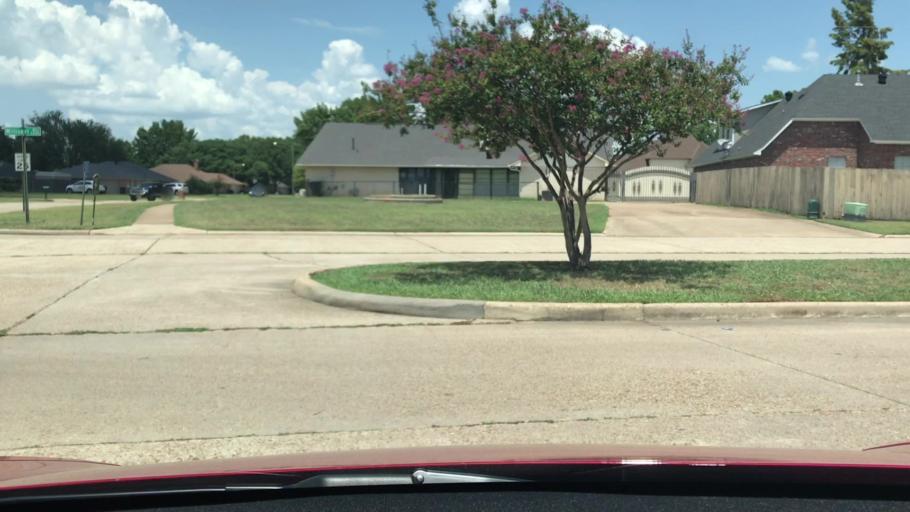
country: US
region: Louisiana
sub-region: Bossier Parish
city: Bossier City
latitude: 32.4279
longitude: -93.7189
